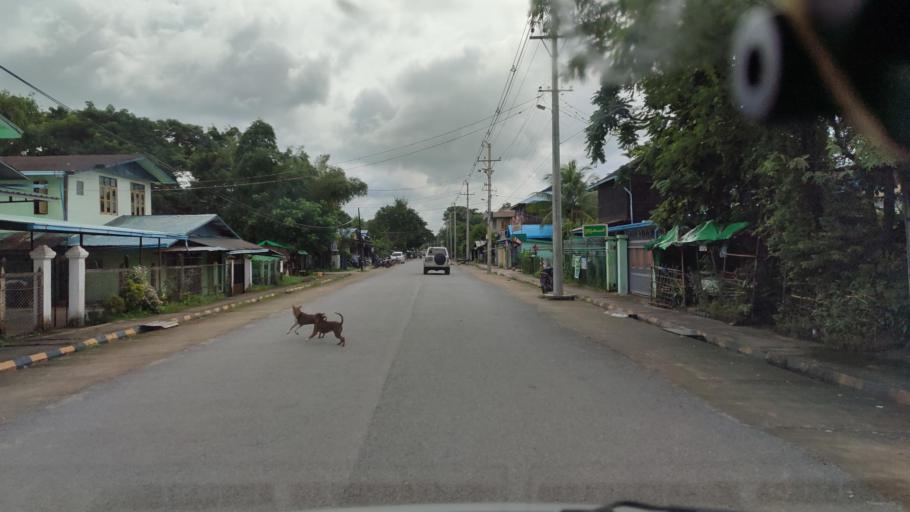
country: MM
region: Bago
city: Thanatpin
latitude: 17.0895
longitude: 96.4603
